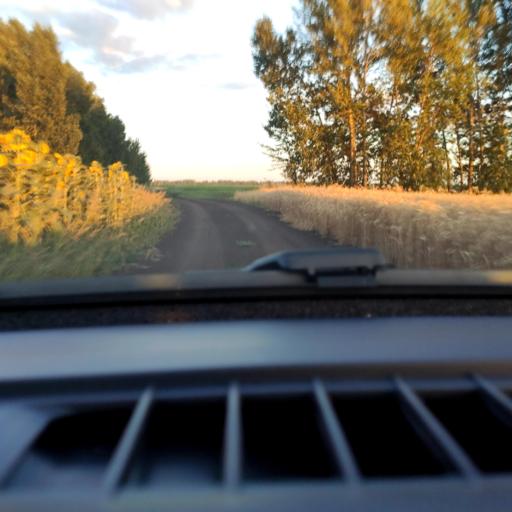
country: RU
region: Voronezj
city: Panino
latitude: 51.5784
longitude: 39.8743
